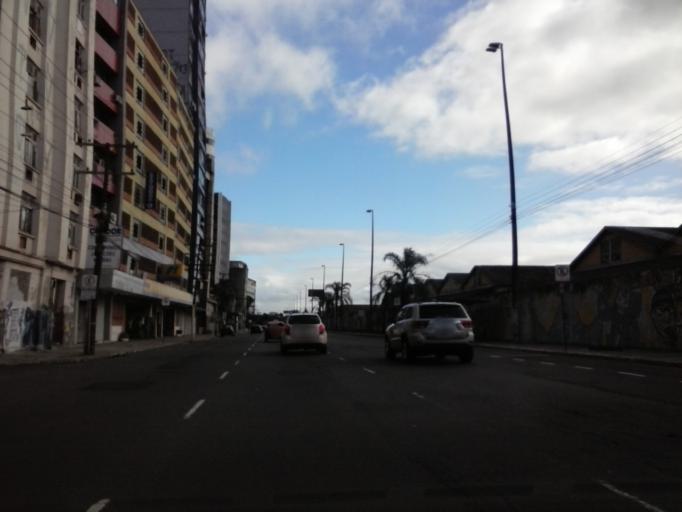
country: BR
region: Rio Grande do Sul
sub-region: Porto Alegre
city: Porto Alegre
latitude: -30.0283
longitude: -51.2329
